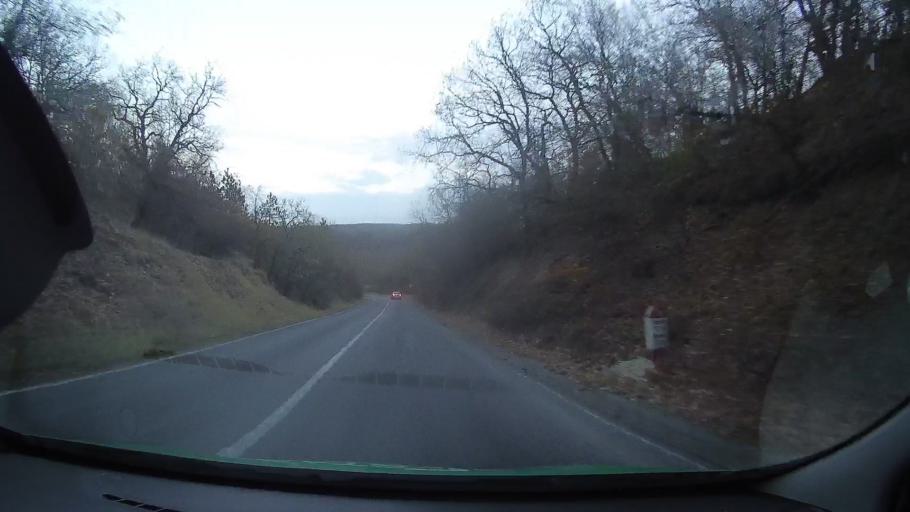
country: RO
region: Constanta
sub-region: Comuna Baneasa
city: Baneasa
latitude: 44.0900
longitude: 27.6542
